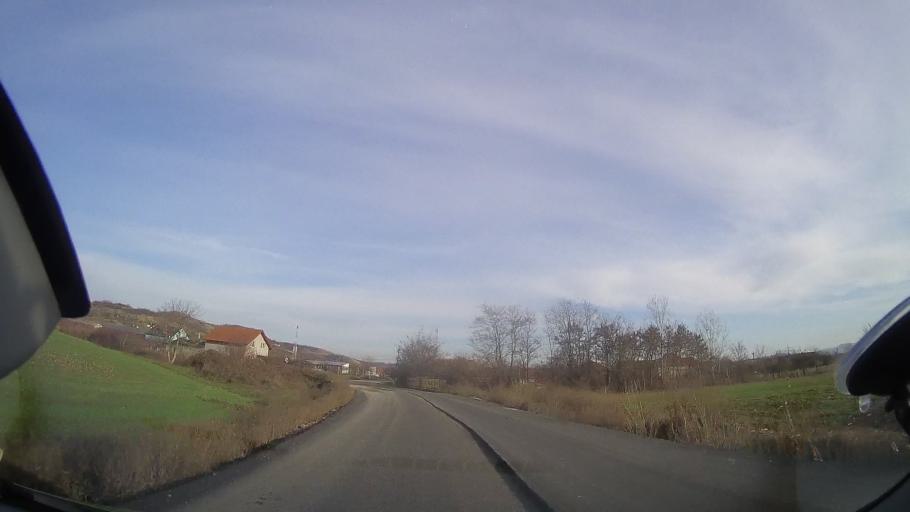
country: RO
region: Bihor
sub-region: Comuna Tileagd
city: Tileagd
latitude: 47.0823
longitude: 22.1947
